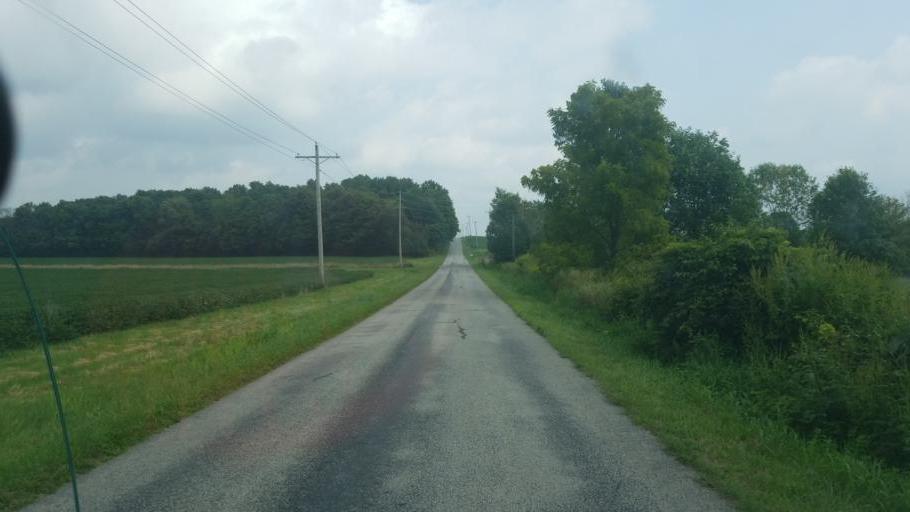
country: US
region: Ohio
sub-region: Huron County
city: Greenwich
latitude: 41.0940
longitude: -82.5254
